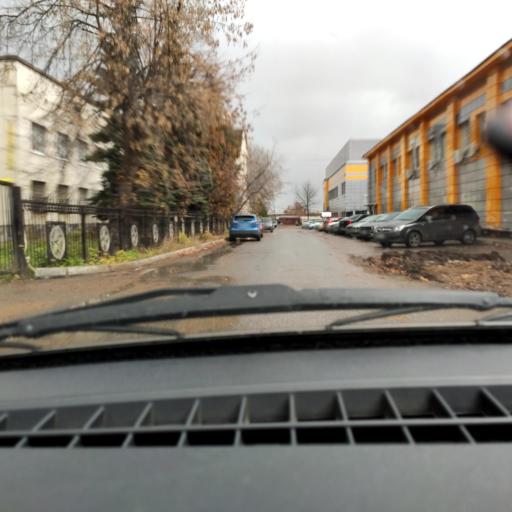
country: RU
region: Bashkortostan
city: Ufa
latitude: 54.8255
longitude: 56.1031
